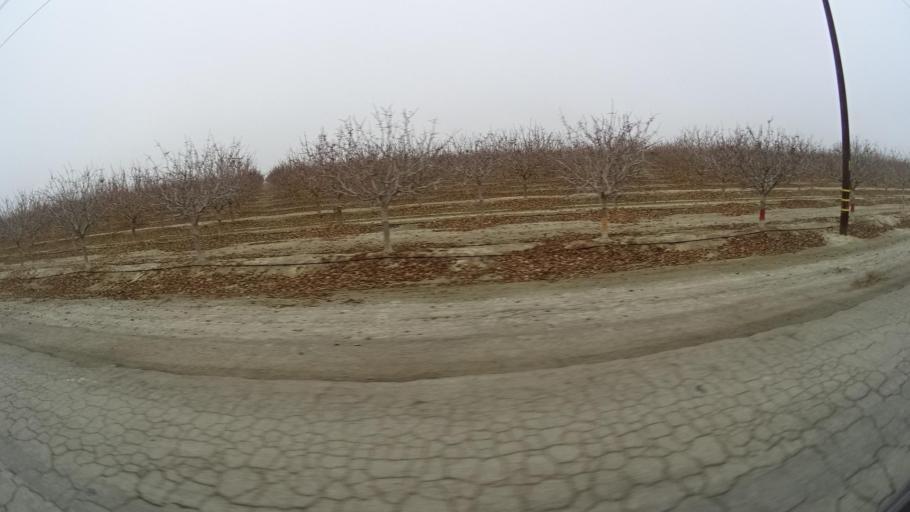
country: US
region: California
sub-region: Tulare County
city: Alpaugh
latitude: 35.7700
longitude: -119.4012
